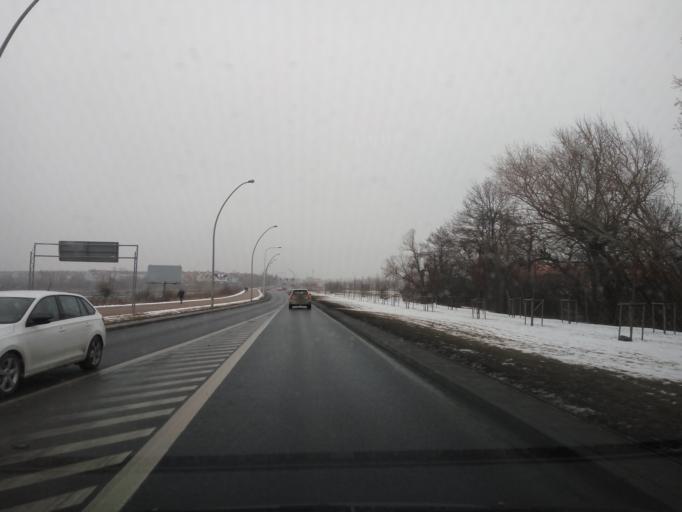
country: PL
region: Lower Silesian Voivodeship
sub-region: Powiat wroclawski
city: Bielany Wroclawskie
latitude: 51.0525
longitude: 16.9655
